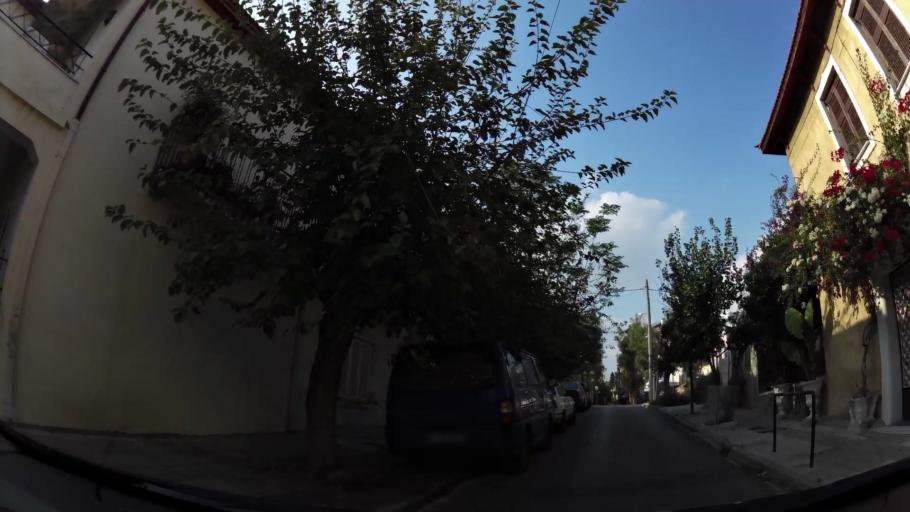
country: GR
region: Attica
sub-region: Nomarchia Athinas
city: Nea Filadelfeia
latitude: 38.0320
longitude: 23.7389
